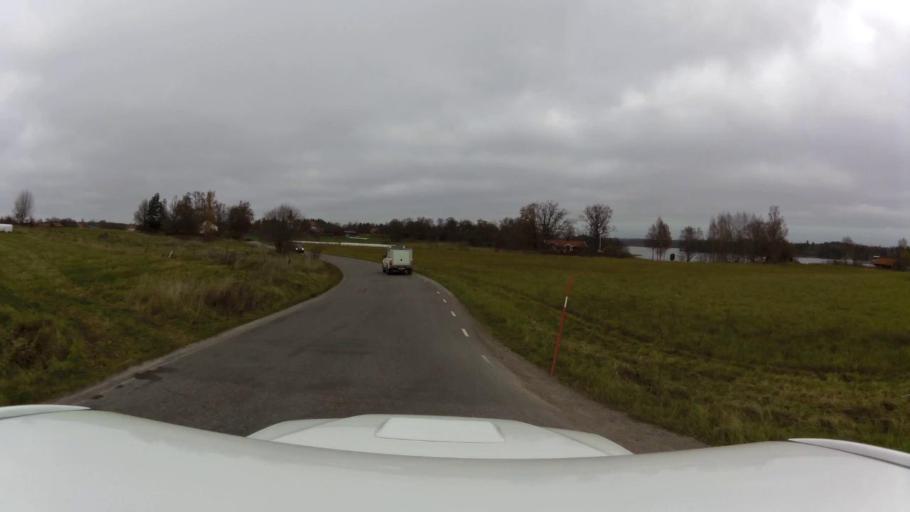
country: SE
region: OEstergoetland
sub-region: Kinda Kommun
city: Rimforsa
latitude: 58.2315
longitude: 15.6896
